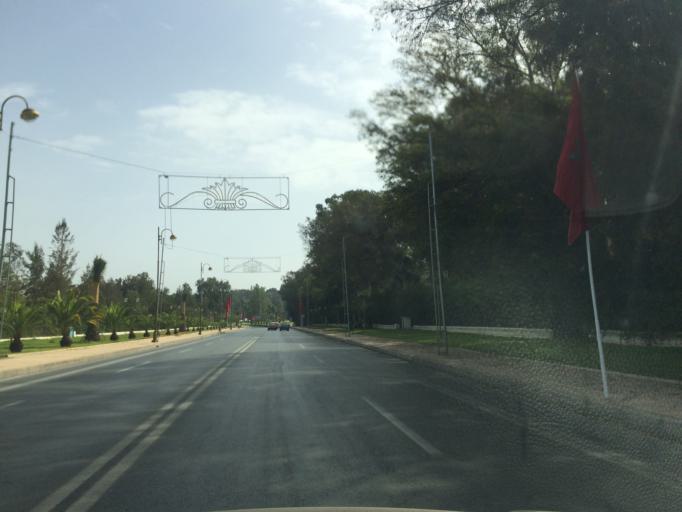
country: MA
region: Rabat-Sale-Zemmour-Zaer
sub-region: Rabat
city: Rabat
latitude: 33.9967
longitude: -6.8368
